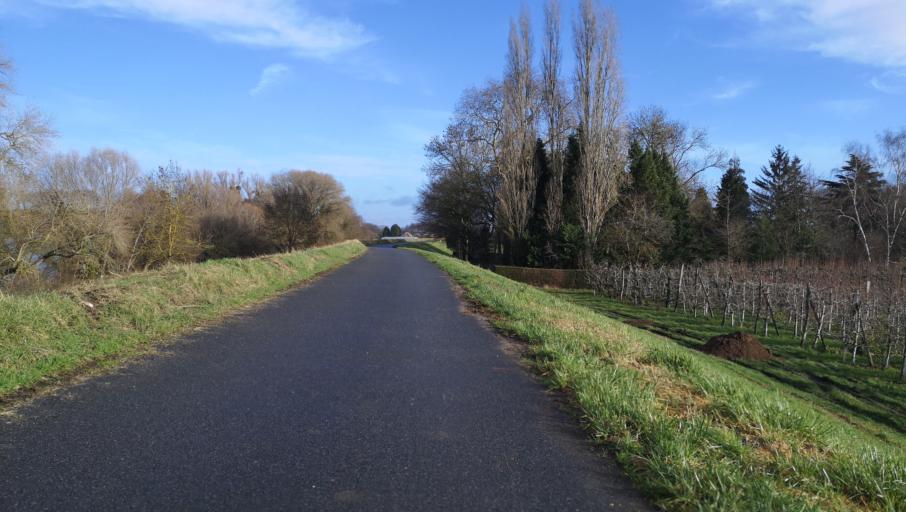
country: FR
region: Centre
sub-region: Departement du Loiret
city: La Chapelle-Saint-Mesmin
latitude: 47.8771
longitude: 1.8349
